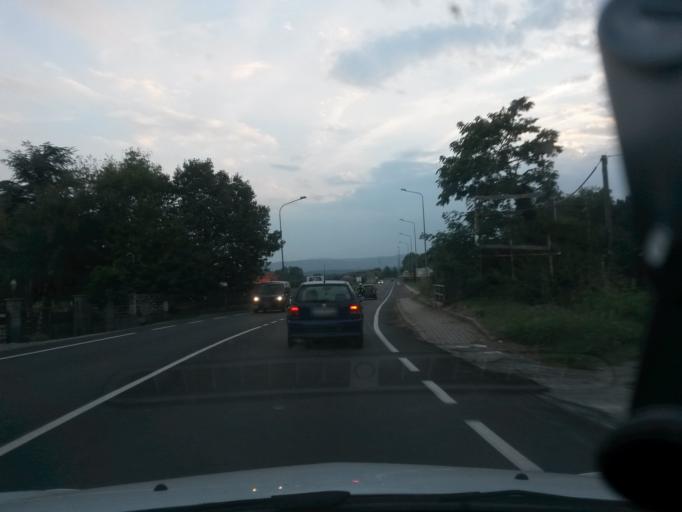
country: IT
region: Piedmont
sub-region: Provincia di Torino
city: Caselette
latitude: 45.1014
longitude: 7.4731
